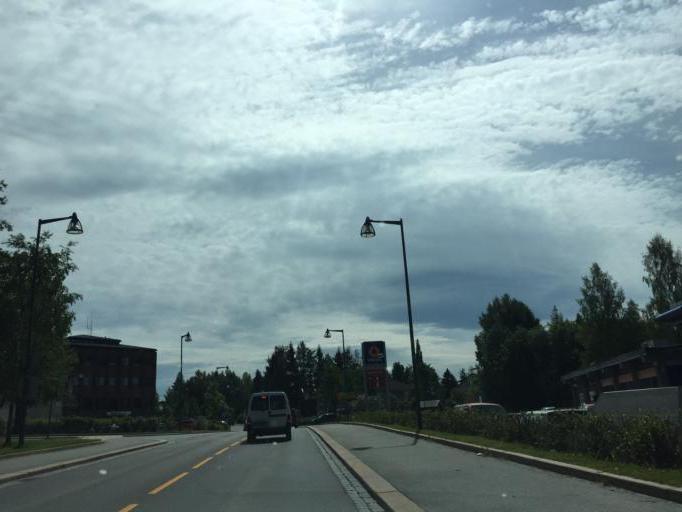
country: NO
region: Akershus
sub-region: Nes
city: Arnes
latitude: 60.1218
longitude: 11.4653
